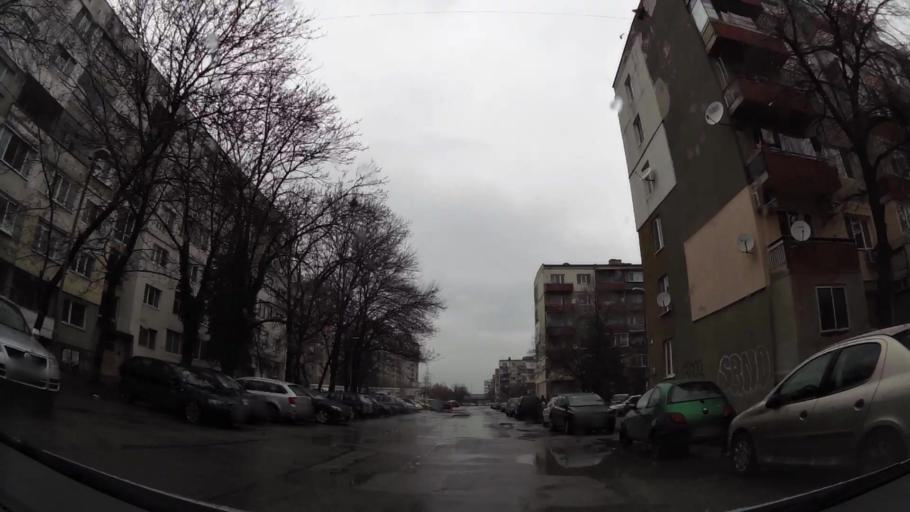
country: BG
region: Sofia-Capital
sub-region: Stolichna Obshtina
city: Sofia
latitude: 42.6624
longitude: 23.3947
